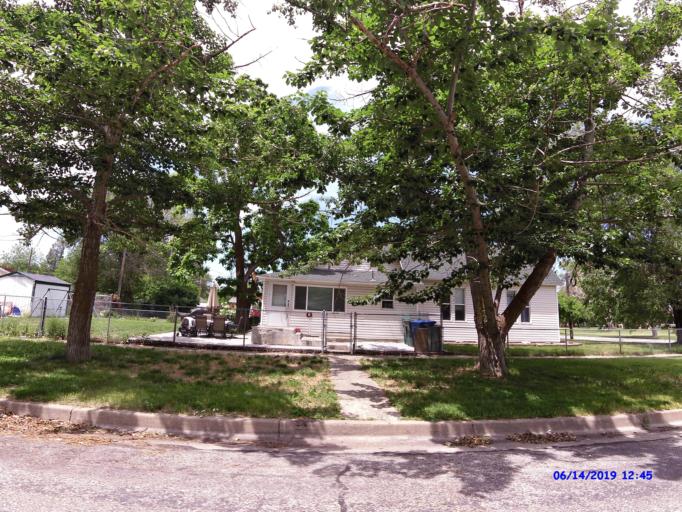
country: US
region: Utah
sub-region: Weber County
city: Ogden
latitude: 41.2308
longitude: -111.9563
